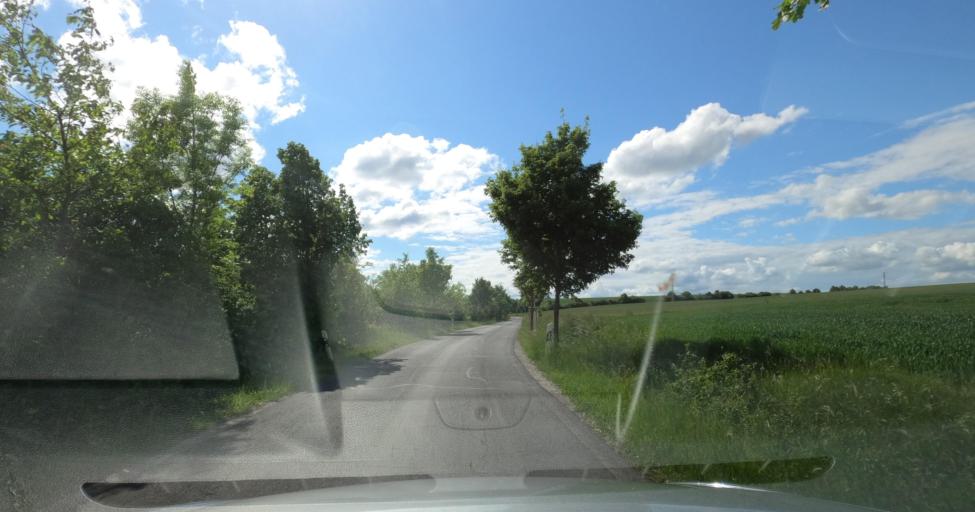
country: DE
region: Thuringia
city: Vollersroda
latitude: 50.9431
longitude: 11.3340
